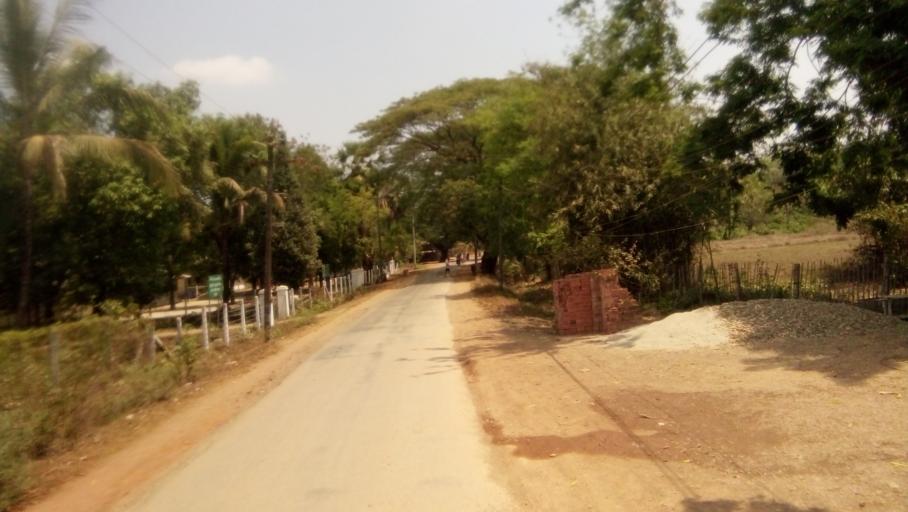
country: MM
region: Kayin
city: Hpa-an
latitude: 17.1303
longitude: 97.8186
